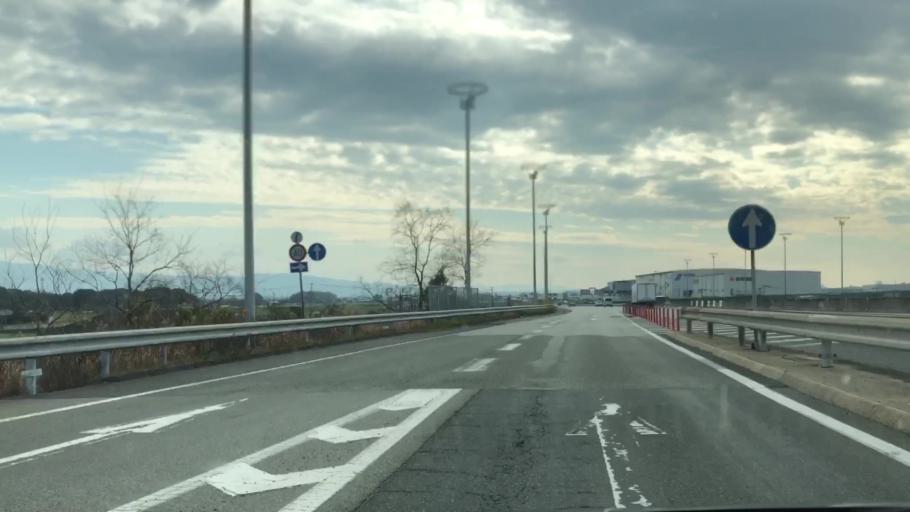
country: JP
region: Saga Prefecture
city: Tosu
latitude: 33.3945
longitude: 130.5386
